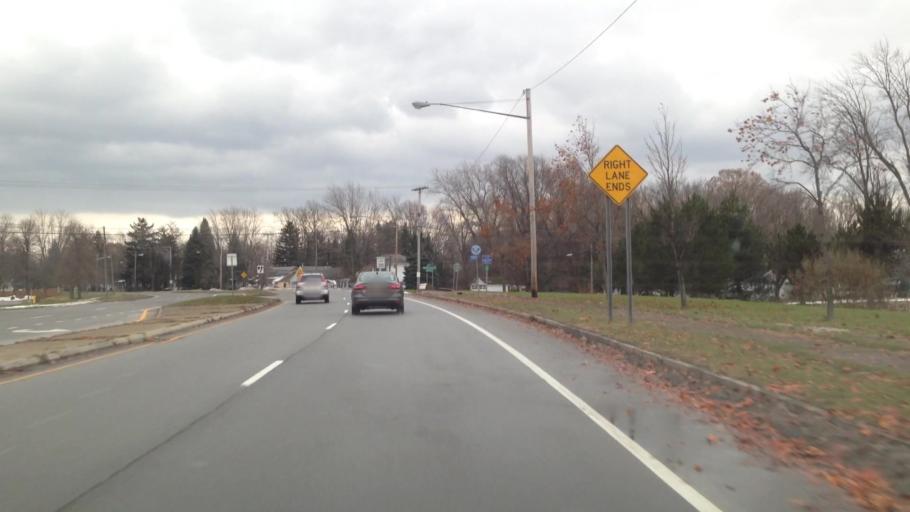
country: US
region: New York
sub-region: Monroe County
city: North Gates
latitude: 43.1313
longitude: -77.6868
